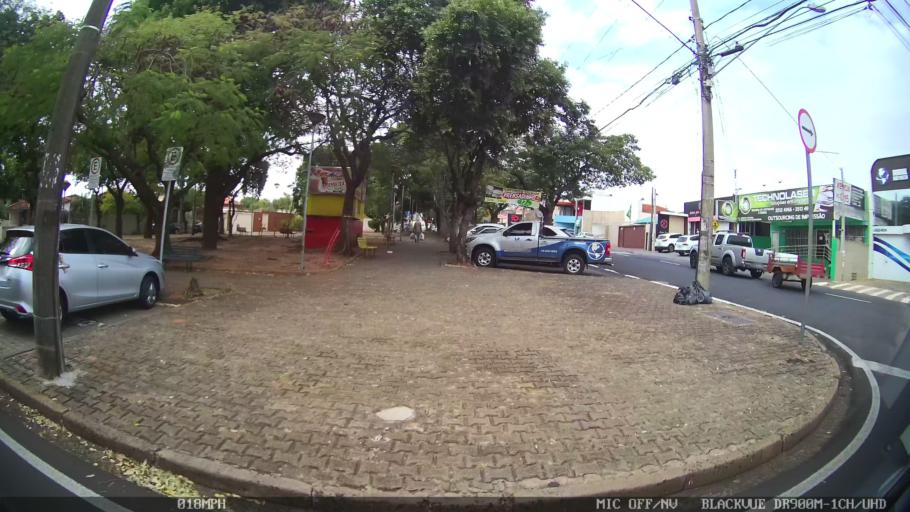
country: BR
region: Sao Paulo
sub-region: Sao Jose Do Rio Preto
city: Sao Jose do Rio Preto
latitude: -20.8158
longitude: -49.3732
